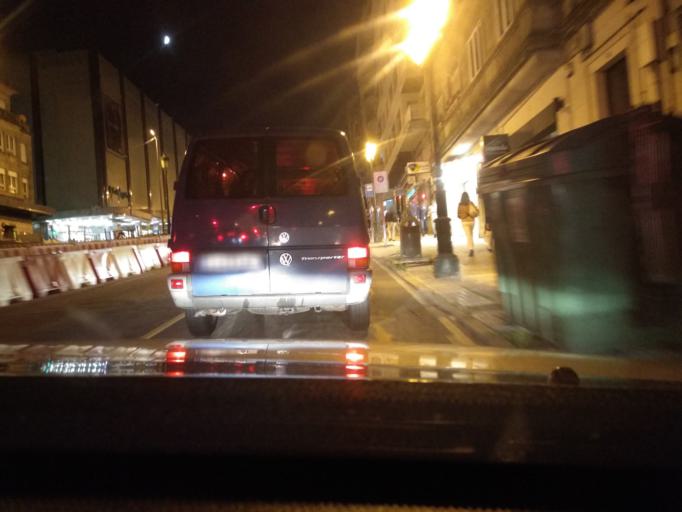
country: ES
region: Galicia
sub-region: Provincia de Pontevedra
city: Vigo
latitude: 42.2334
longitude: -8.7174
